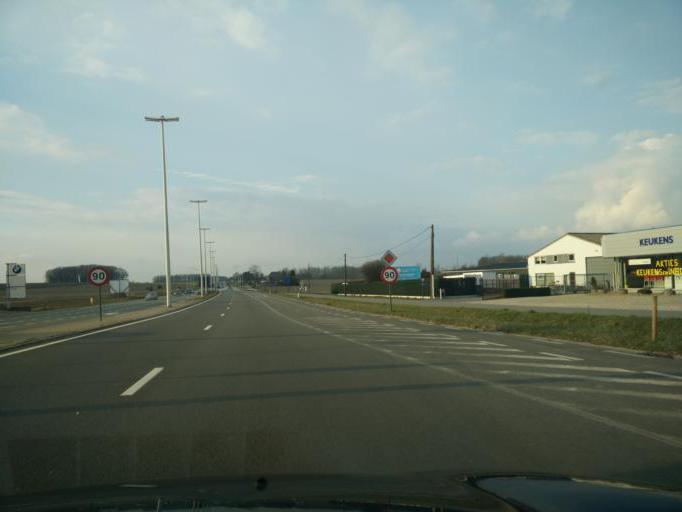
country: BE
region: Flanders
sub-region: Provincie Oost-Vlaanderen
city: Perre
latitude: 50.8986
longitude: 3.8291
